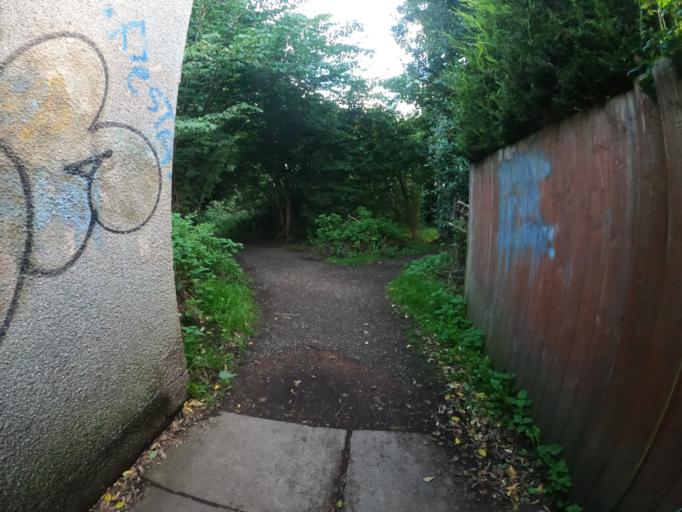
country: GB
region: Scotland
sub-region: Edinburgh
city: Colinton
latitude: 55.9619
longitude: -3.2885
